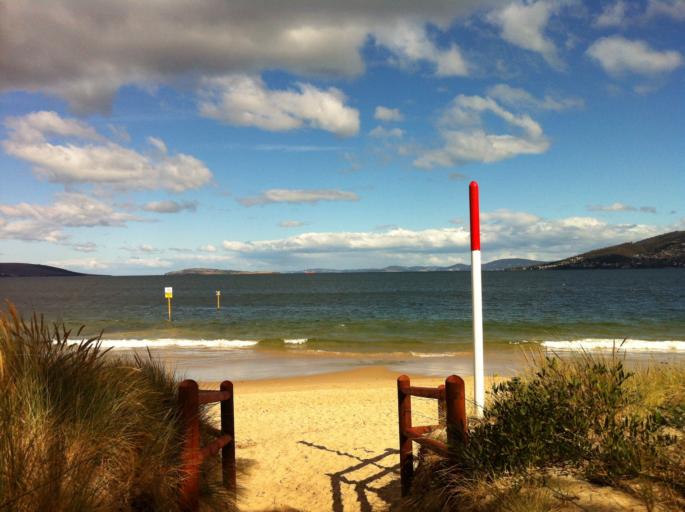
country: AU
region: Tasmania
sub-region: Clarence
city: Bellerive
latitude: -42.8791
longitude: 147.3822
